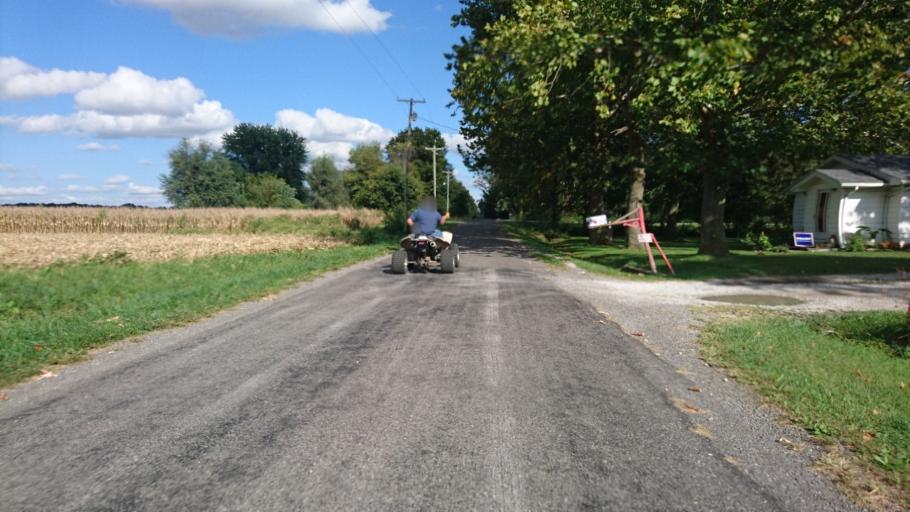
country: US
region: Illinois
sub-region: Macoupin County
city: Staunton
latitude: 38.9902
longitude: -89.7276
